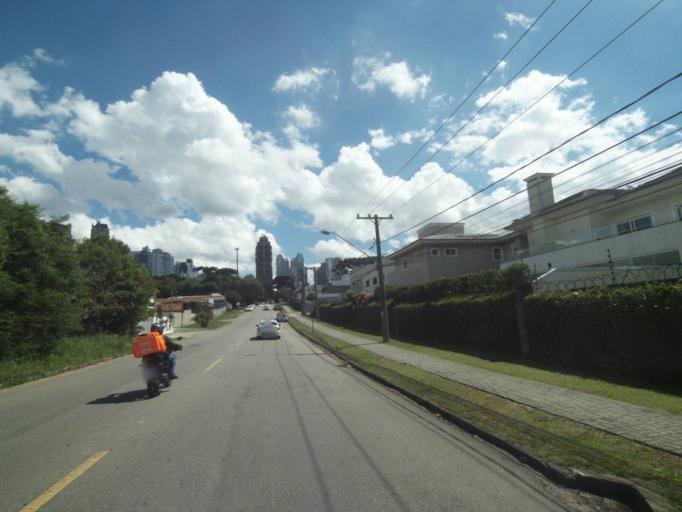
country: BR
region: Parana
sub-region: Curitiba
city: Curitiba
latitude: -25.4331
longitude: -49.3346
